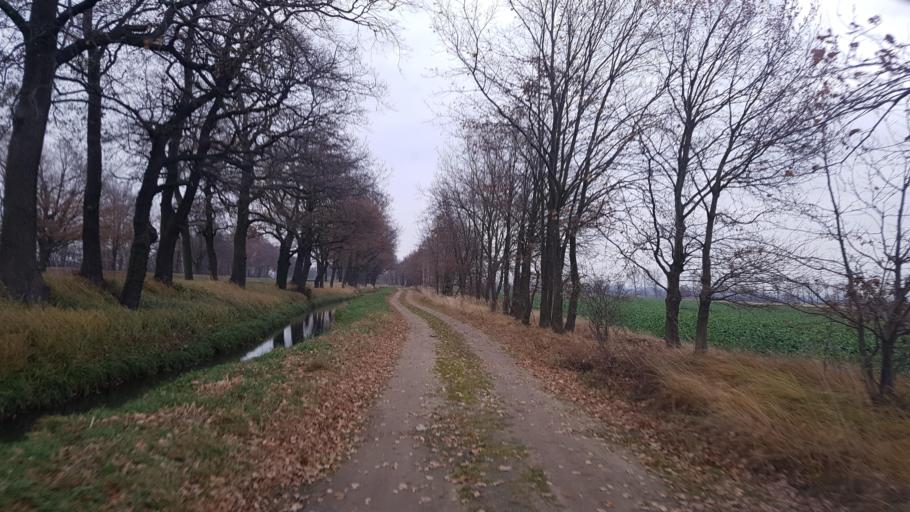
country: DE
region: Brandenburg
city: Hirschfeld
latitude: 51.4131
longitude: 13.6139
